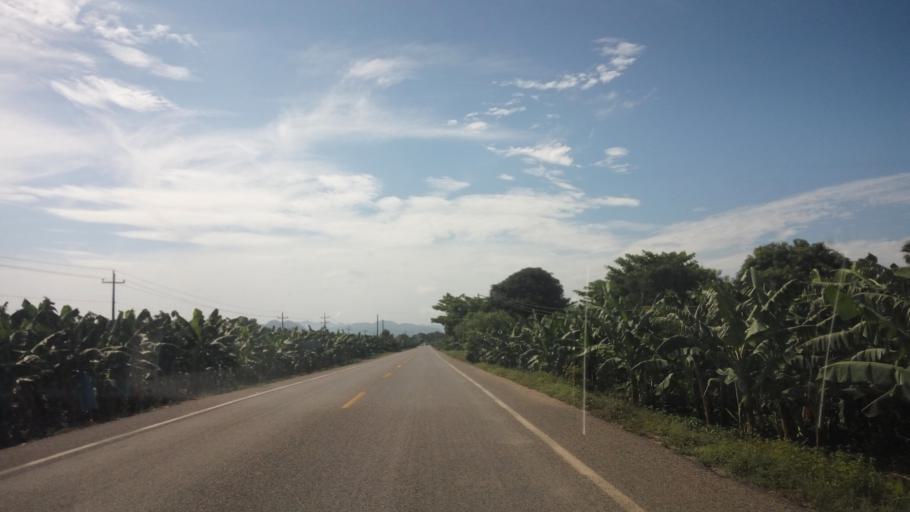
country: MX
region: Tabasco
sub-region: Teapa
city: Eureka y Belen
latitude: 17.6369
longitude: -92.9673
